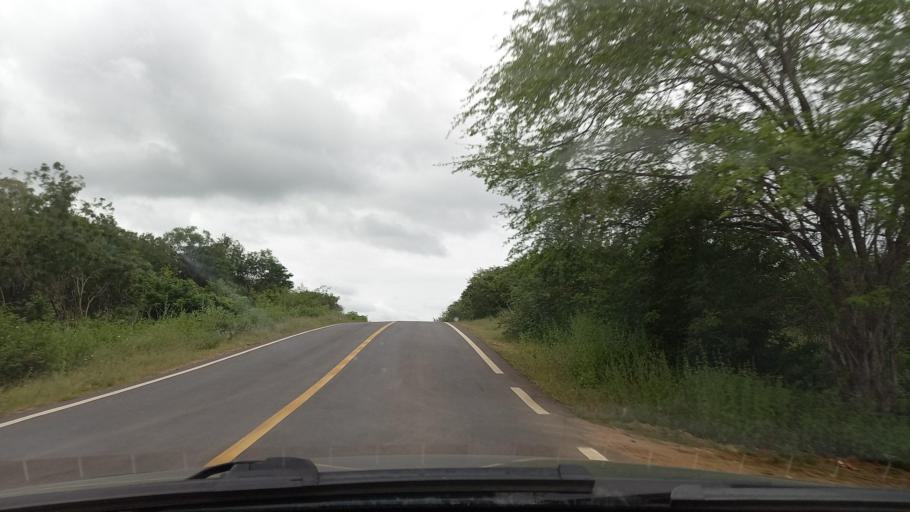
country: BR
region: Sergipe
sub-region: Caninde De Sao Francisco
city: Caninde de Sao Francisco
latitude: -9.6170
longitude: -37.7746
